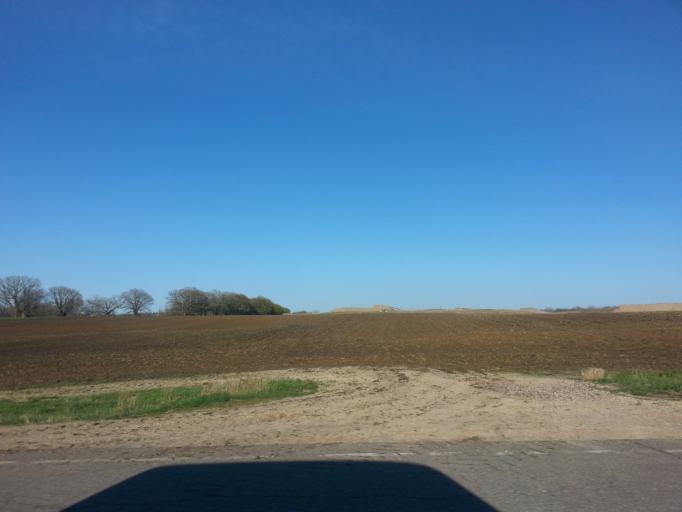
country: US
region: Minnesota
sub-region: Dakota County
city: Lakeville
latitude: 44.6136
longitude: -93.2630
